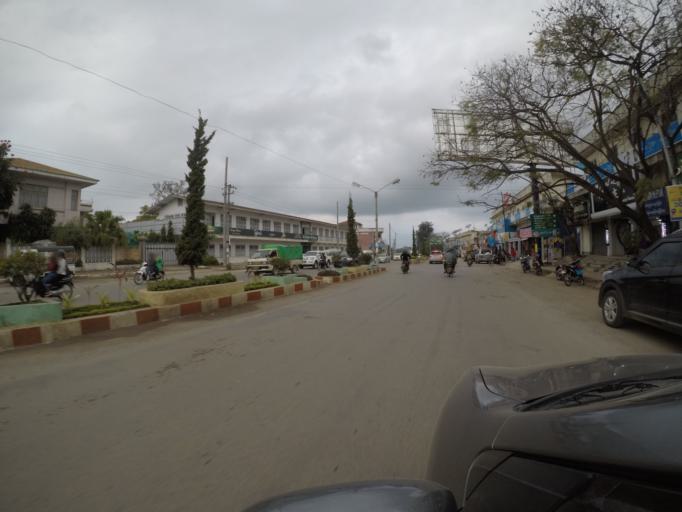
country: MM
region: Shan
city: Taunggyi
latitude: 20.7939
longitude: 97.0374
